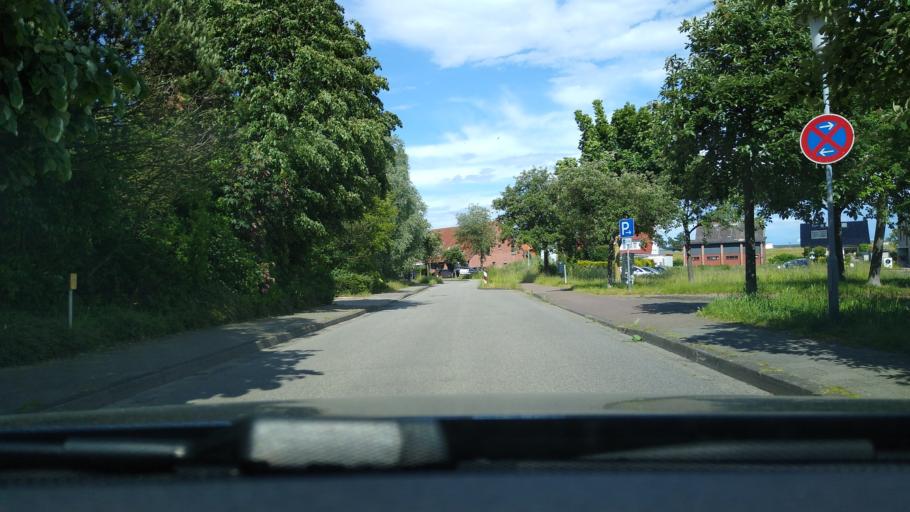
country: DE
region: Schleswig-Holstein
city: Dahme
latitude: 54.2272
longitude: 11.0830
